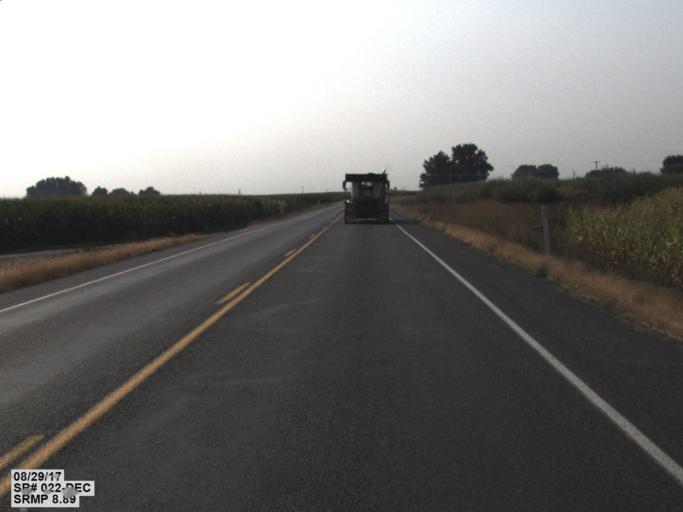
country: US
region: Washington
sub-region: Yakima County
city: Granger
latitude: 46.3257
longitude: -120.2408
